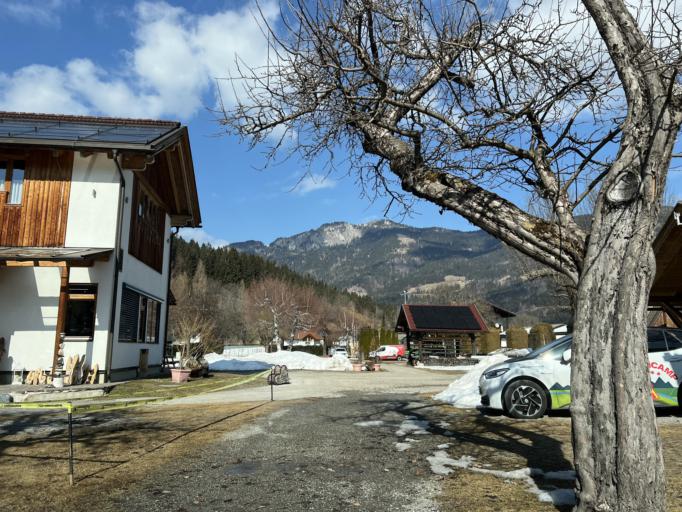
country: AT
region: Carinthia
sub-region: Politischer Bezirk Spittal an der Drau
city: Oberdrauburg
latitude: 46.6694
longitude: 12.9913
